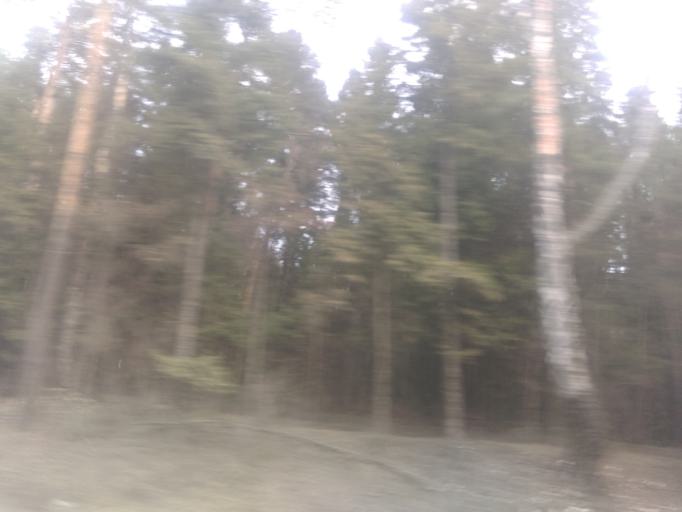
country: RU
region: Moskovskaya
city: Tuchkovo
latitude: 55.5659
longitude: 36.5242
